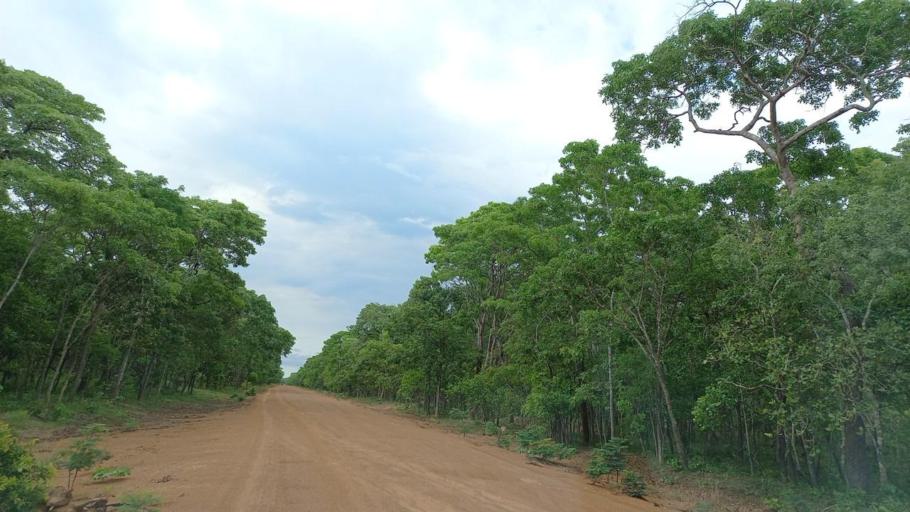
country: ZM
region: North-Western
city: Kalengwa
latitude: -13.3748
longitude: 25.0733
